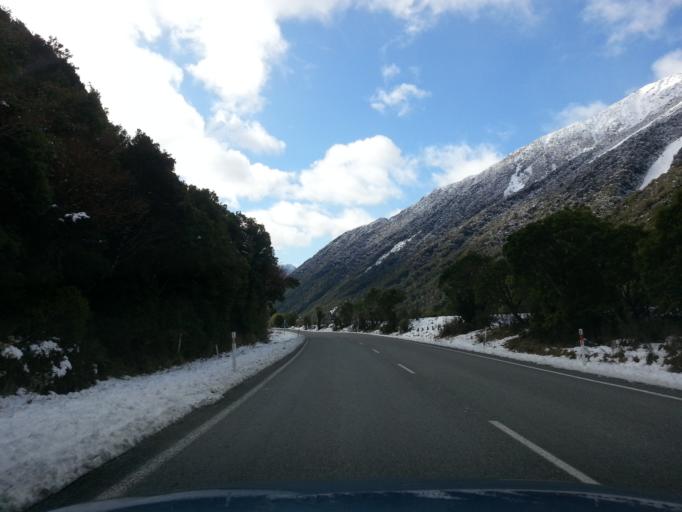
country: NZ
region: West Coast
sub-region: Grey District
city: Greymouth
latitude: -42.8475
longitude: 171.5590
